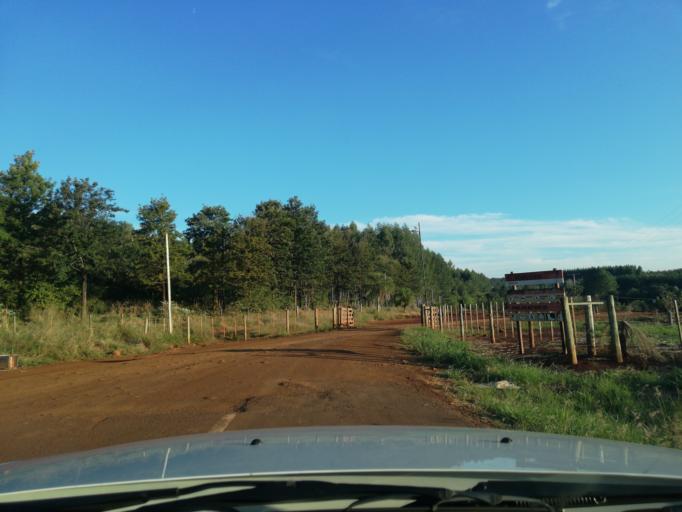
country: AR
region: Misiones
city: Garupa
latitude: -27.4672
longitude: -55.9190
